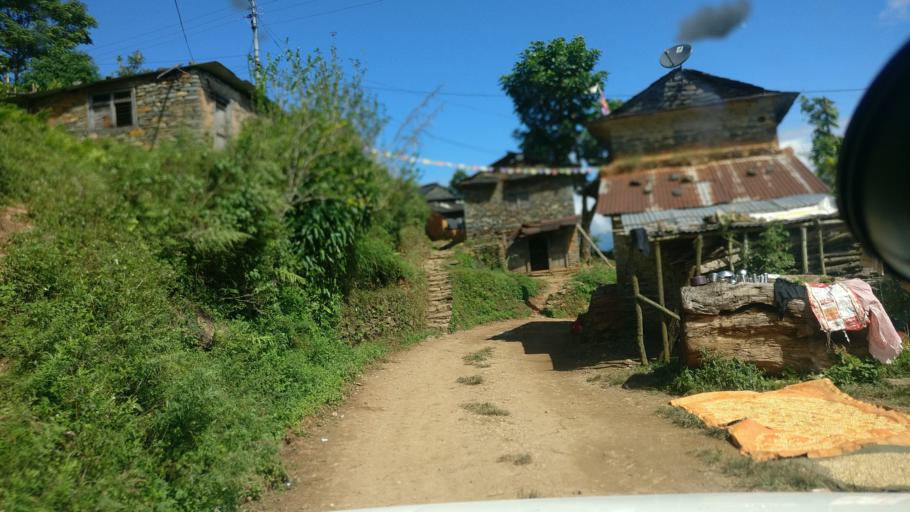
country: NP
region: Western Region
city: Baglung
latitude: 28.1267
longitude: 83.6667
